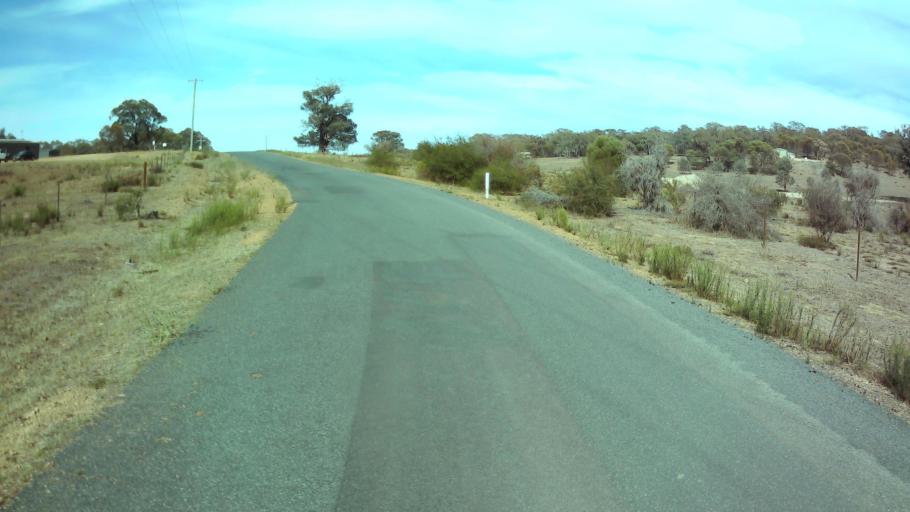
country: AU
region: New South Wales
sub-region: Weddin
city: Grenfell
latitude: -33.8776
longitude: 148.1999
